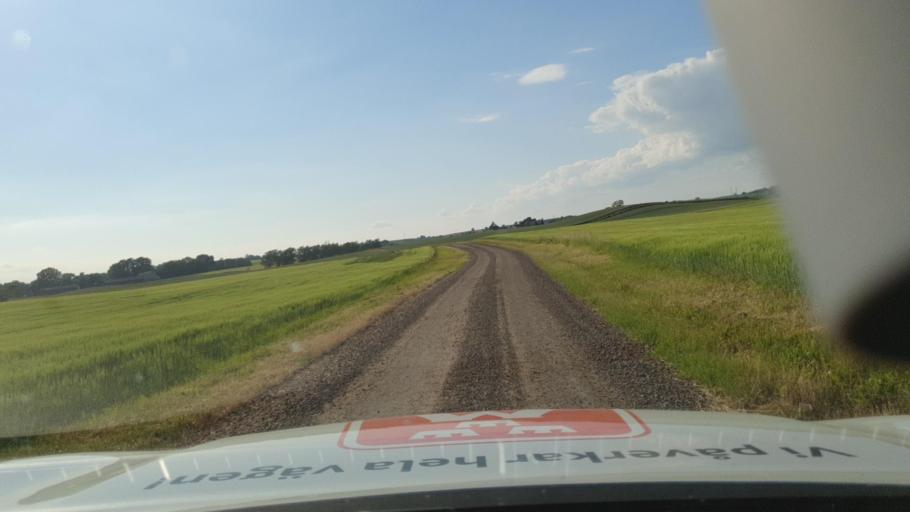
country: SE
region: Skane
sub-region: Skurups Kommun
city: Rydsgard
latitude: 55.4875
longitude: 13.5900
